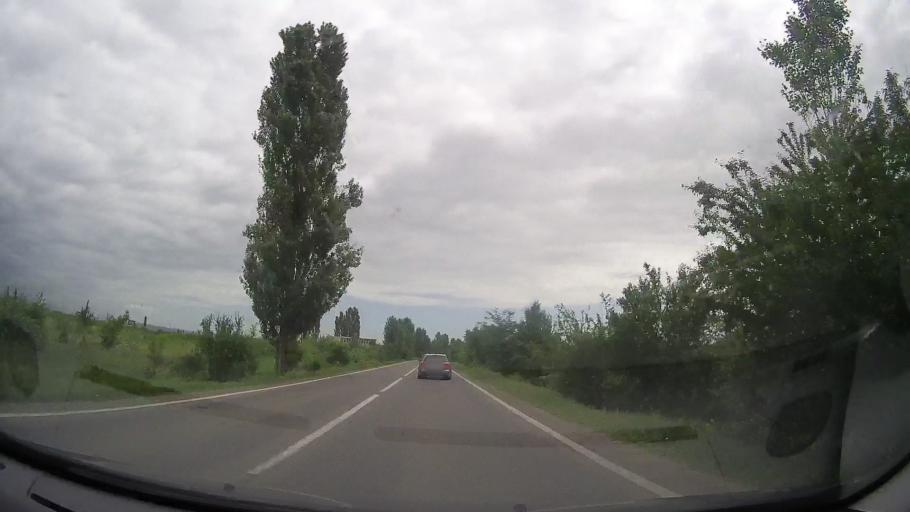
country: RO
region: Prahova
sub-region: Comuna Barcanesti
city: Barcanesti
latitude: 44.8923
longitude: 26.0501
